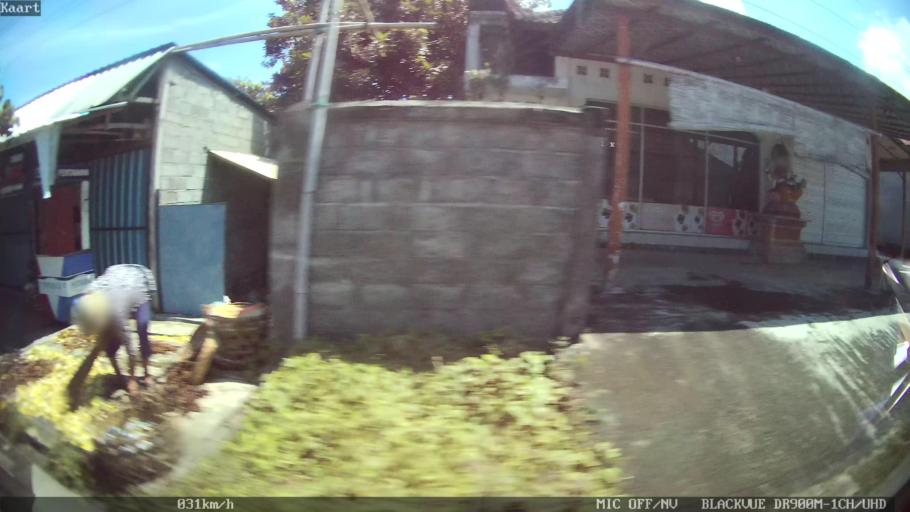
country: ID
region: Bali
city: Banjar Kelodan
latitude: -8.5524
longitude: 115.3353
